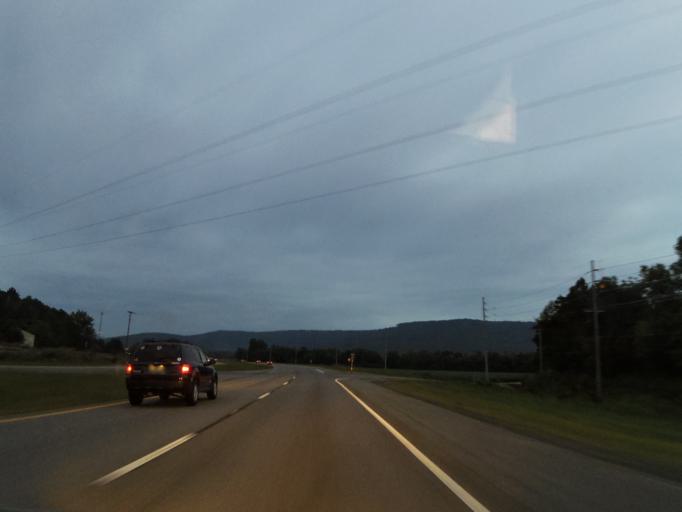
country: US
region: Alabama
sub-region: Madison County
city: Owens Cross Roads
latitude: 34.7053
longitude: -86.3960
